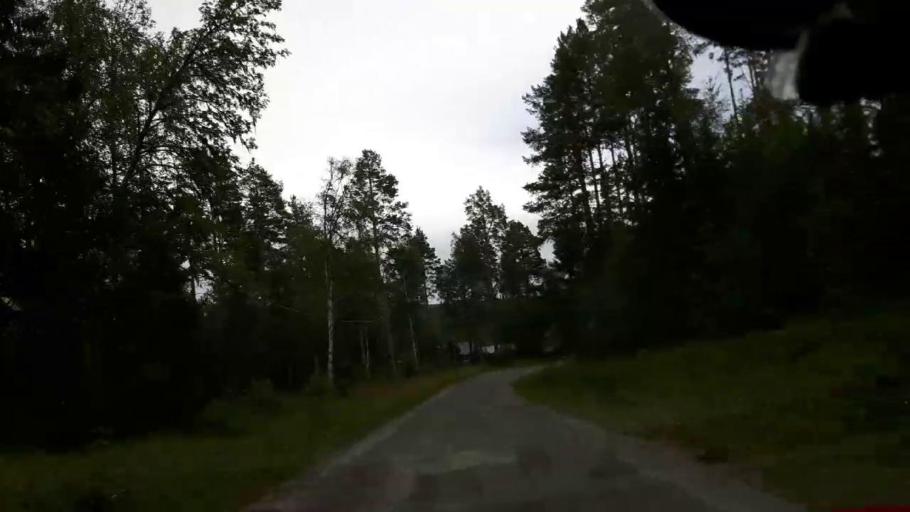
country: SE
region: Jaemtland
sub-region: Braecke Kommun
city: Braecke
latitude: 62.8911
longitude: 15.6071
